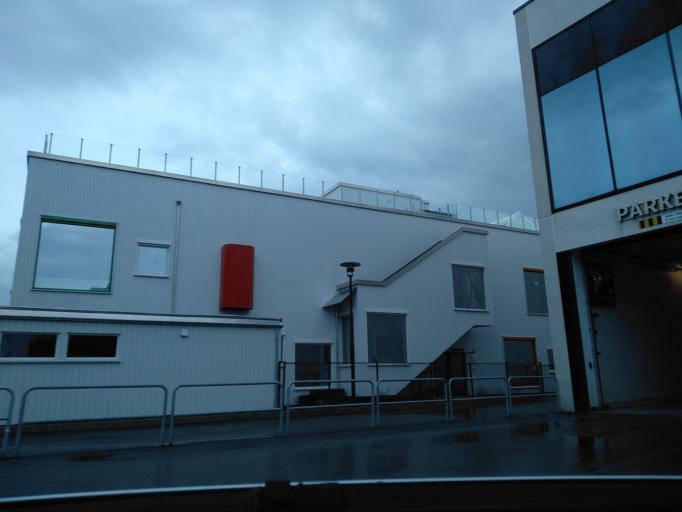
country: NO
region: Rogaland
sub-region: Stavanger
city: Stavanger
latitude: 58.9841
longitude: 5.6896
